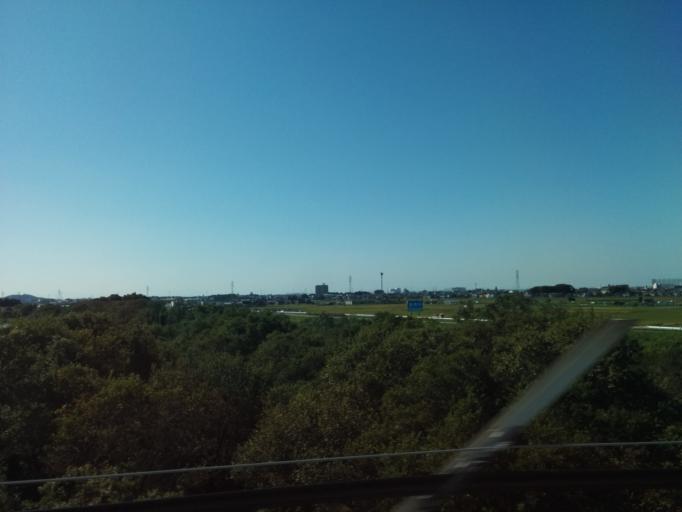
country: JP
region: Aichi
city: Anjo
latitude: 34.9173
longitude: 137.1082
